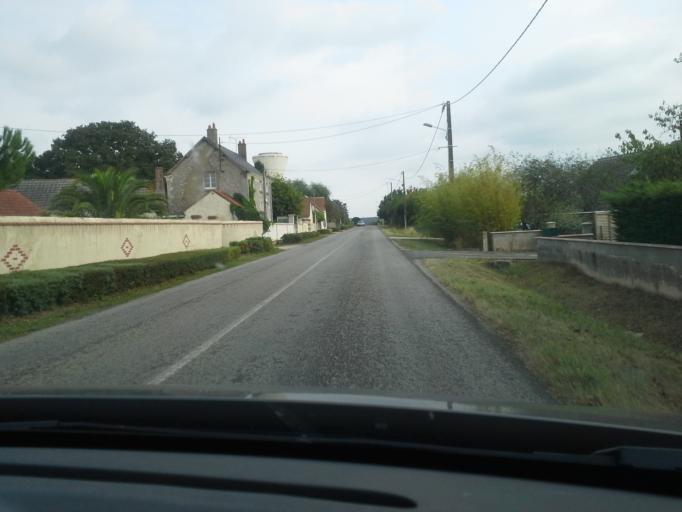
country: FR
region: Centre
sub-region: Departement du Loir-et-Cher
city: Herbault
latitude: 47.5927
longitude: 1.1935
